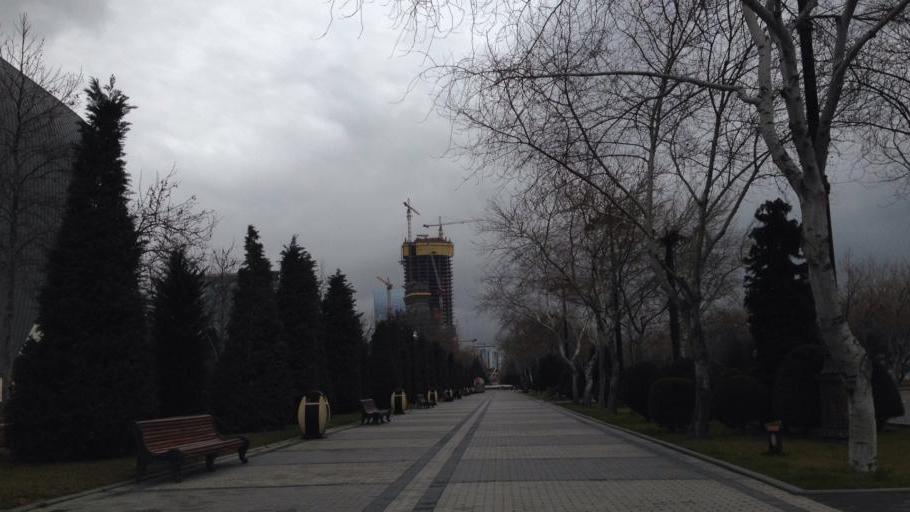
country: AZ
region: Baki
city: Baku
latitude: 40.3703
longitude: 49.8500
